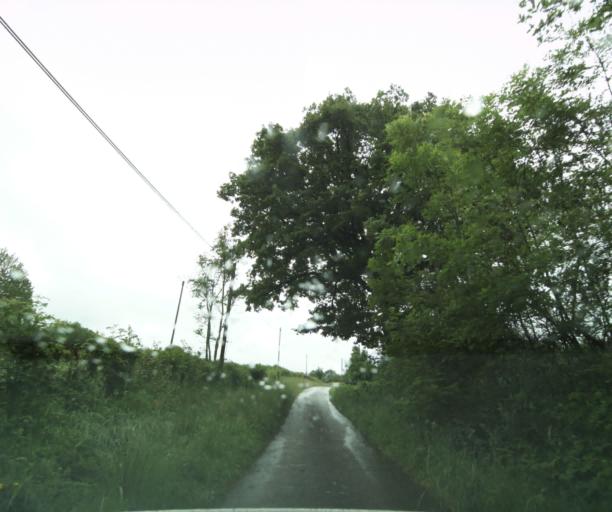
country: FR
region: Bourgogne
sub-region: Departement de Saone-et-Loire
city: Charolles
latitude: 46.5005
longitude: 4.3931
